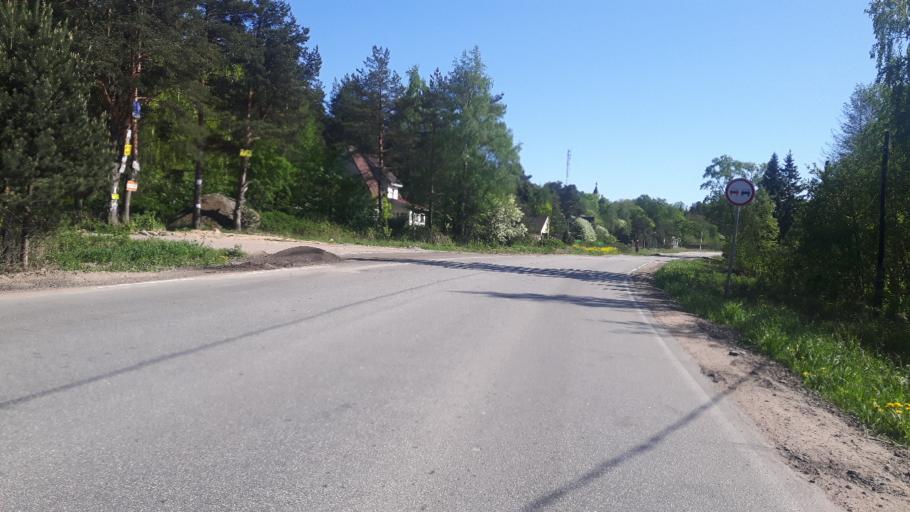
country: RU
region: Leningrad
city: Sosnovyy Bor
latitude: 60.2216
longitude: 29.0093
